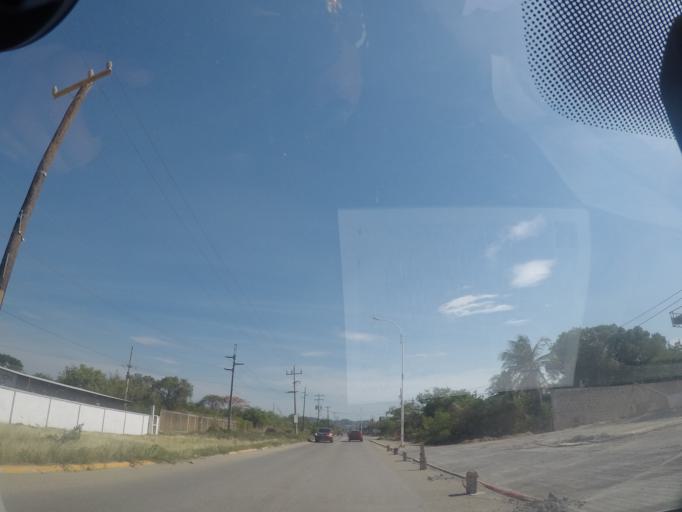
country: MX
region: Oaxaca
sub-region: Salina Cruz
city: Salina Cruz
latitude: 16.2183
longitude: -95.1908
